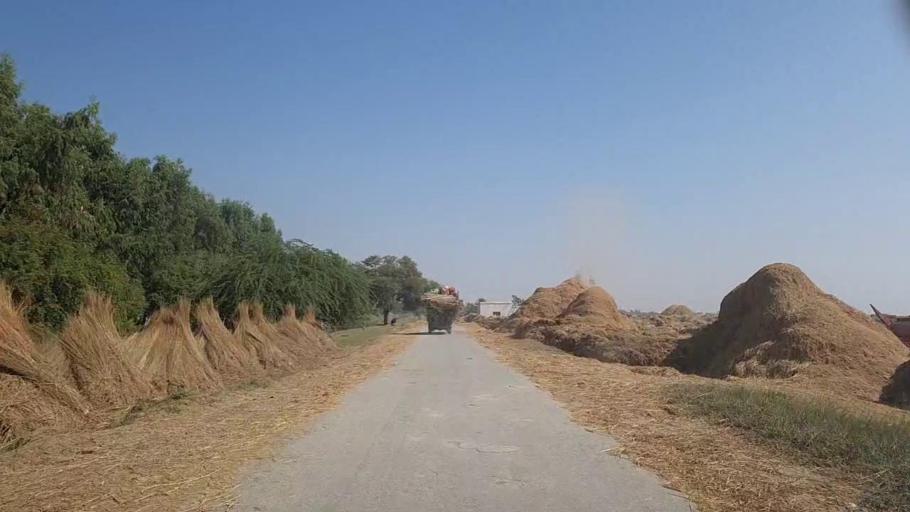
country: PK
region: Sindh
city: Thul
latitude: 28.2421
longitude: 68.7986
